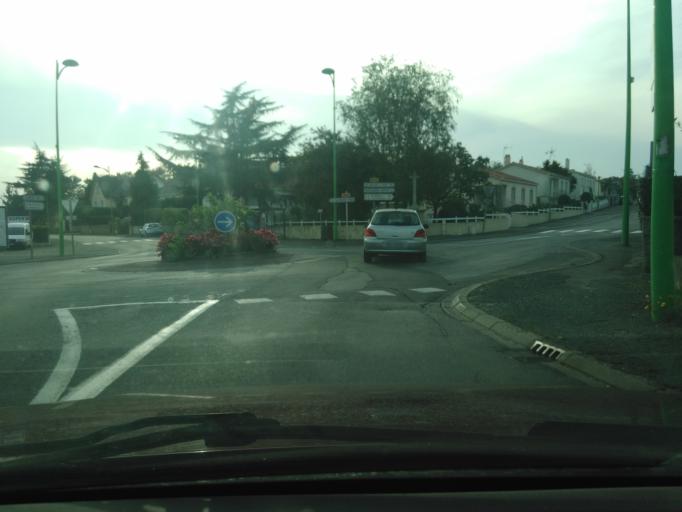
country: FR
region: Pays de la Loire
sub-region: Departement de la Vendee
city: Dompierre-sur-Yon
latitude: 46.7353
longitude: -1.3892
